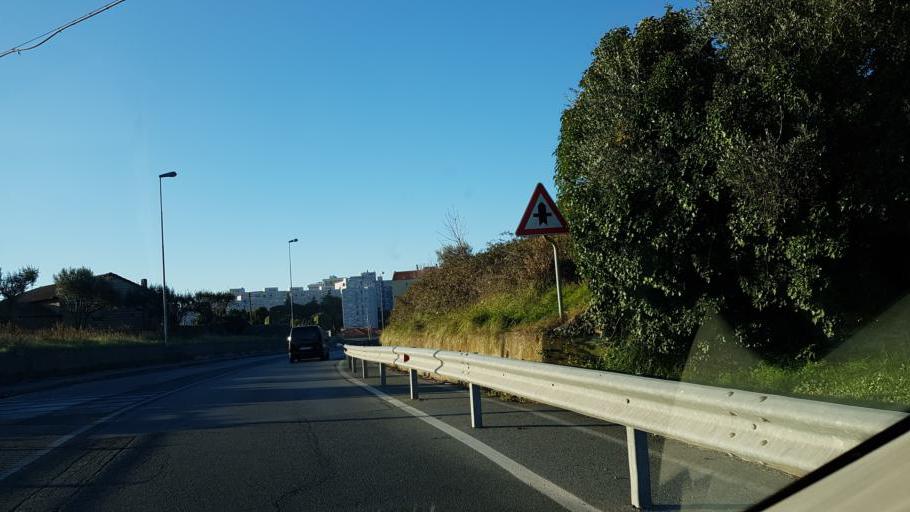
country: IT
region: Liguria
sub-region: Provincia di Savona
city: Valleggia
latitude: 44.2972
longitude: 8.4492
